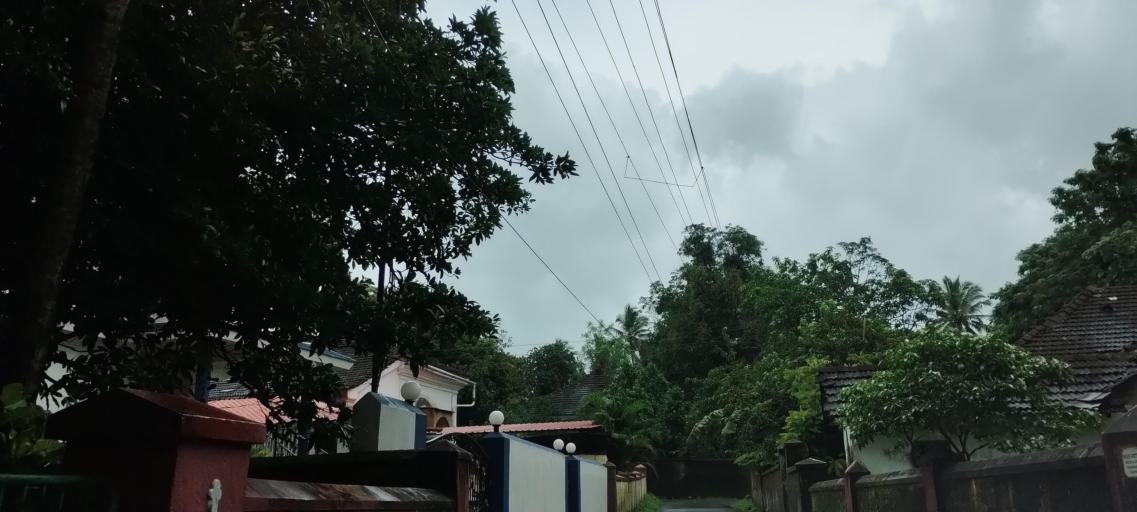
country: IN
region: Goa
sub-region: North Goa
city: Aldona
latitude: 15.5852
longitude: 73.8677
